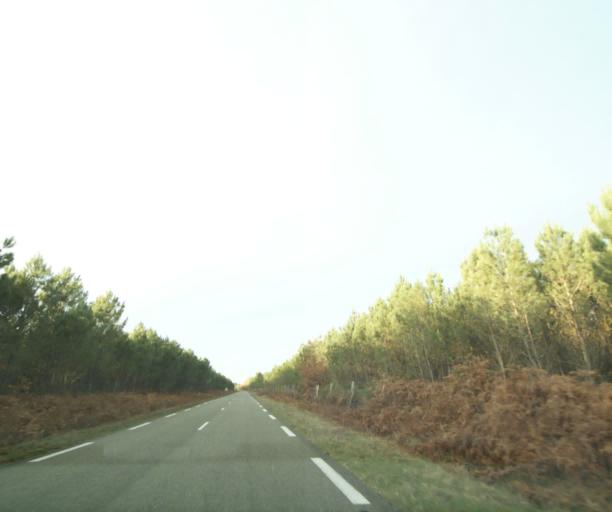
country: FR
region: Aquitaine
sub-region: Departement des Landes
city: Gabarret
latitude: 44.1170
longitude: -0.1050
